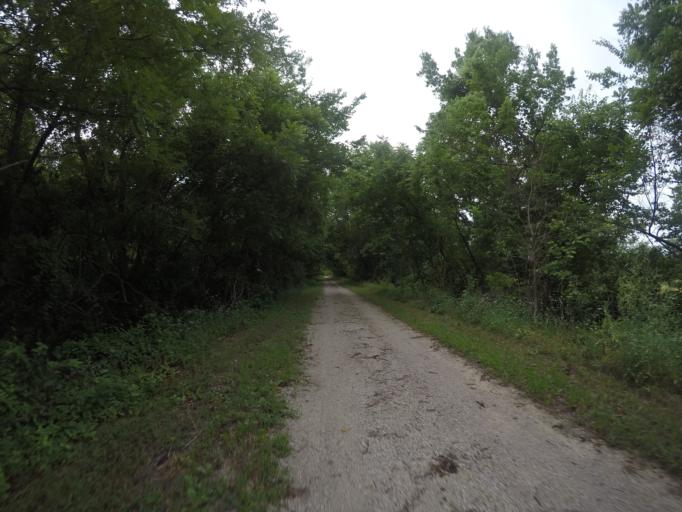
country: US
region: Kansas
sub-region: Franklin County
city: Ottawa
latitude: 38.4781
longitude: -95.2749
